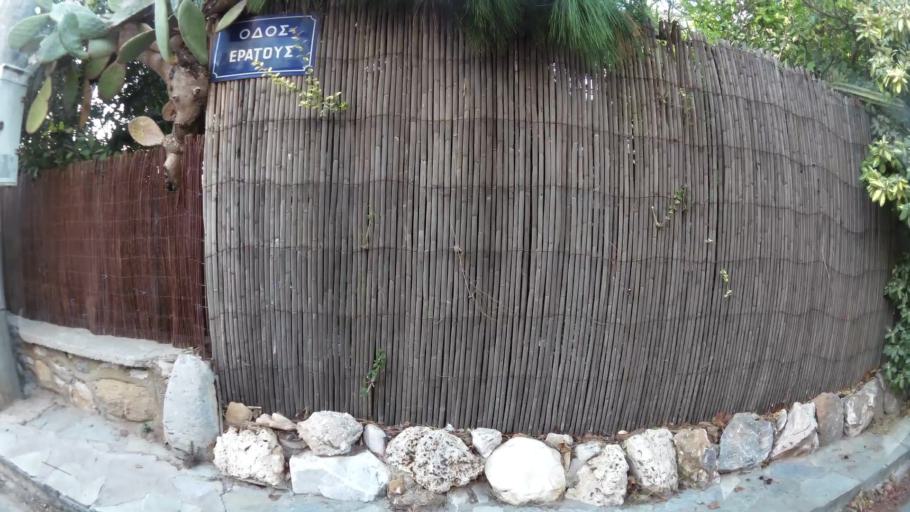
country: GR
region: Attica
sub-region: Nomarchia Anatolikis Attikis
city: Rafina
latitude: 38.0147
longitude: 24.0160
